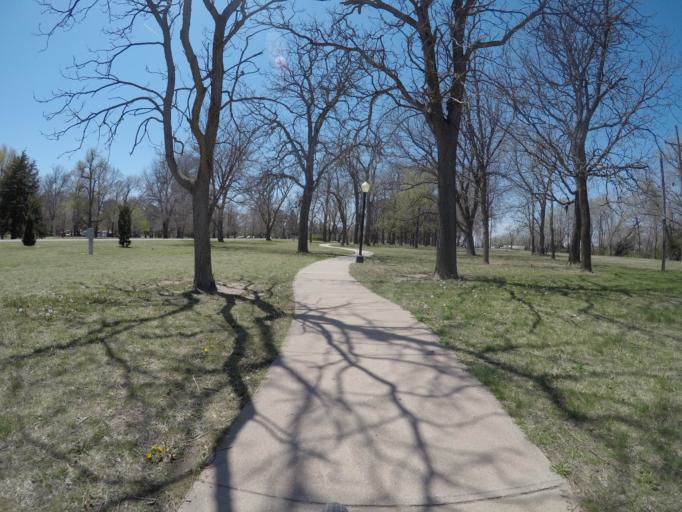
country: US
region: Kansas
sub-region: Pratt County
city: Pratt
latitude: 37.6363
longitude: -98.7337
